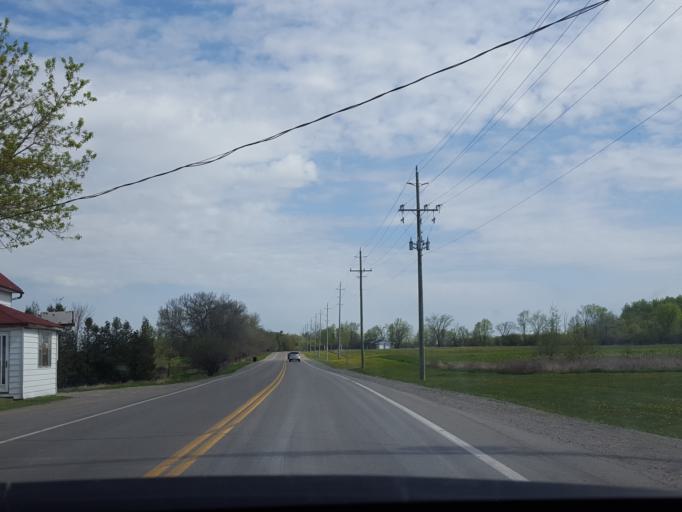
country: CA
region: Ontario
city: Uxbridge
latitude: 44.1703
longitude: -78.8944
